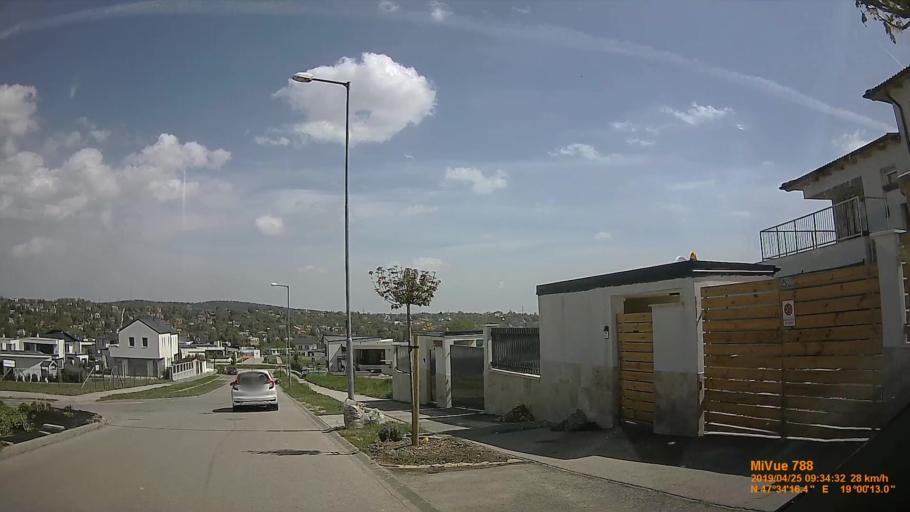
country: HU
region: Pest
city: Urom
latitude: 47.5712
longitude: 19.0033
